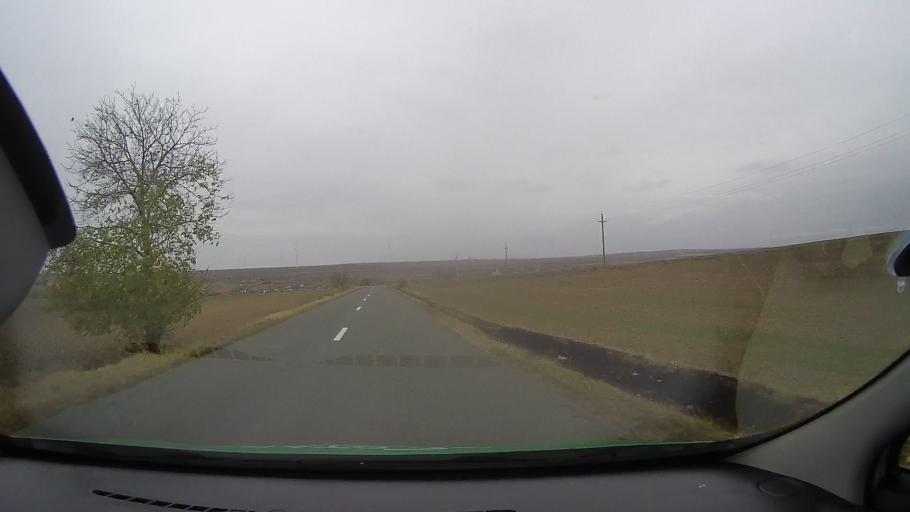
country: RO
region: Constanta
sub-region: Comuna Targusor
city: Targusor
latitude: 44.4862
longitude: 28.3667
